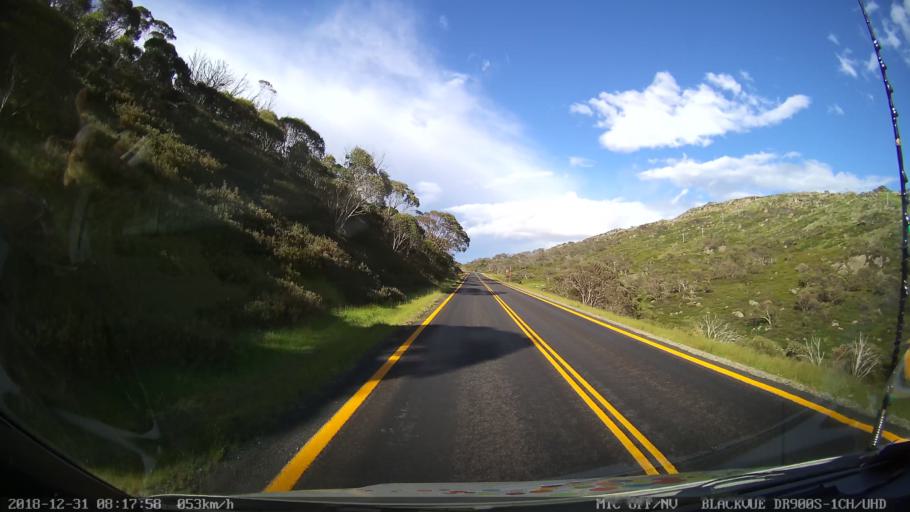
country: AU
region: New South Wales
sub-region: Snowy River
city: Jindabyne
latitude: -36.4121
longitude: 148.3995
